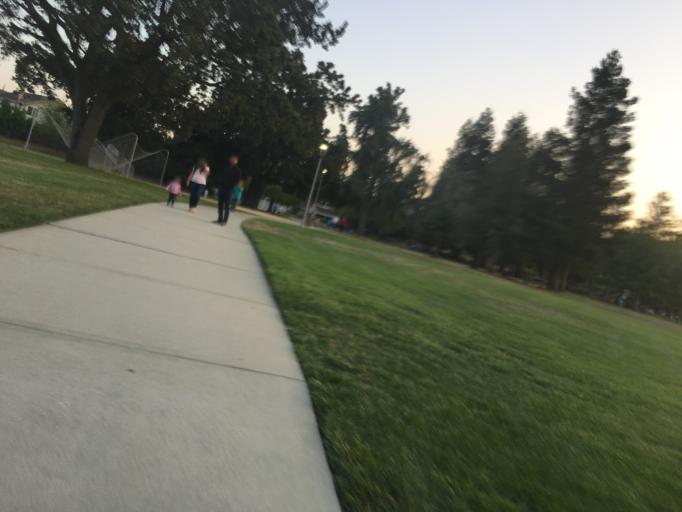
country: US
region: California
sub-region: Santa Clara County
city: Cupertino
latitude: 37.3107
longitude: -122.0393
